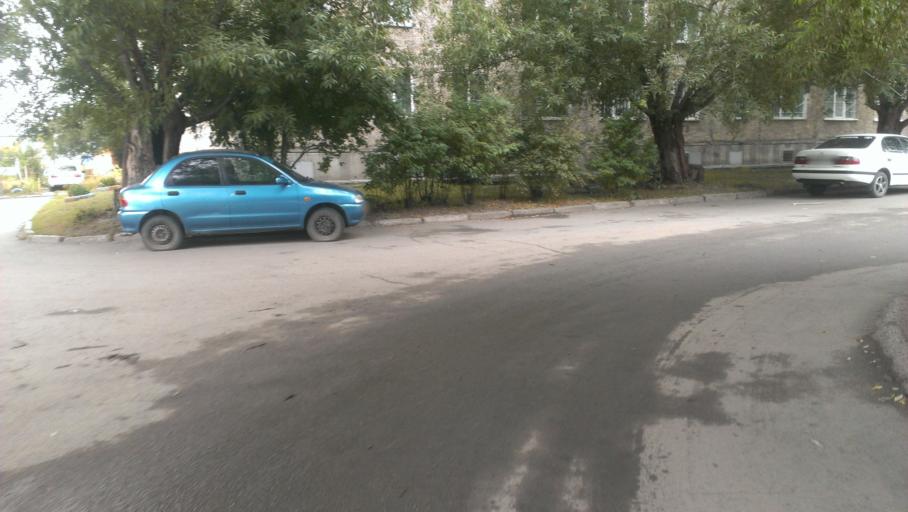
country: RU
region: Altai Krai
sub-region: Gorod Barnaulskiy
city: Barnaul
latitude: 53.3710
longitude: 83.6885
